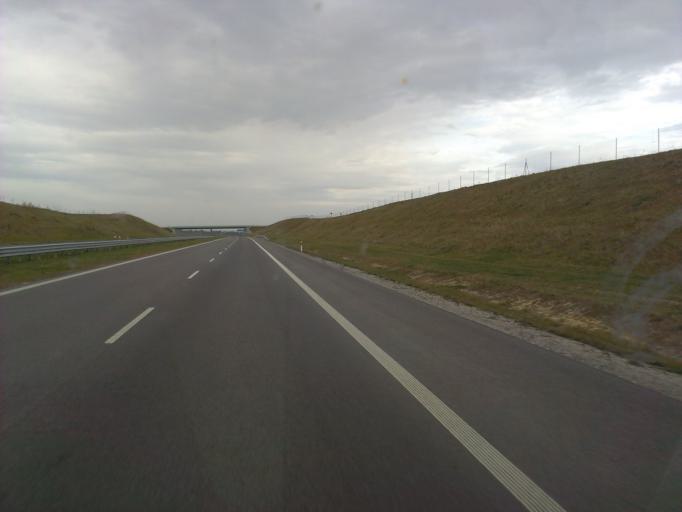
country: PL
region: Subcarpathian Voivodeship
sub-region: Powiat jaroslawski
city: Wierzbna
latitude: 50.0074
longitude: 22.5977
